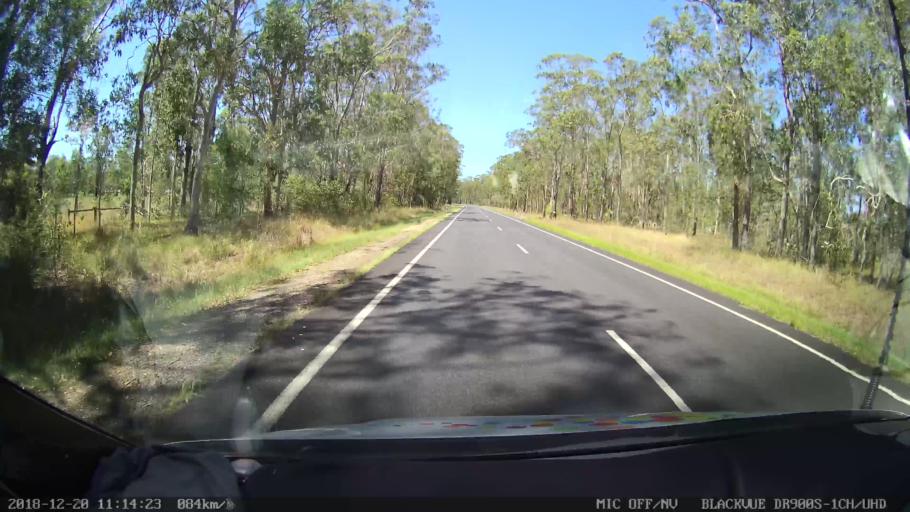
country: AU
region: New South Wales
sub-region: Richmond Valley
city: Casino
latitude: -29.0000
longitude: 153.0090
